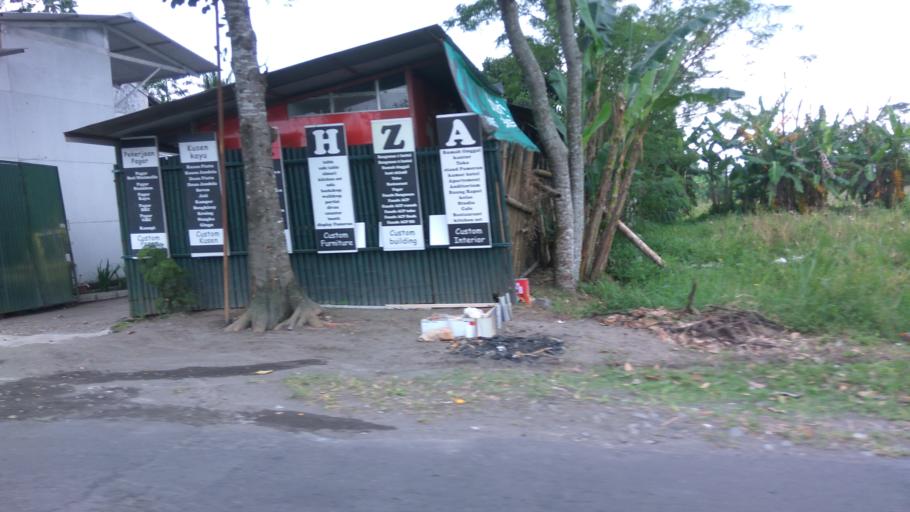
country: ID
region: Daerah Istimewa Yogyakarta
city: Melati
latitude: -7.7267
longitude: 110.4036
